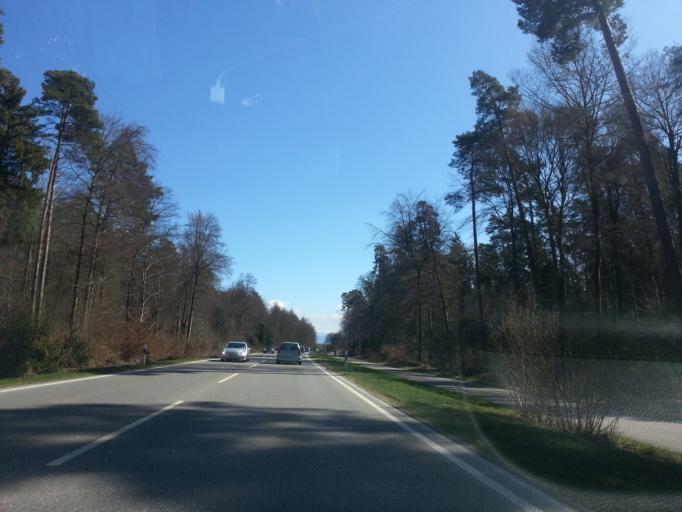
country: DE
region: Baden-Wuerttemberg
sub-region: Tuebingen Region
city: Eriskirch
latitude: 47.6213
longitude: 9.5595
